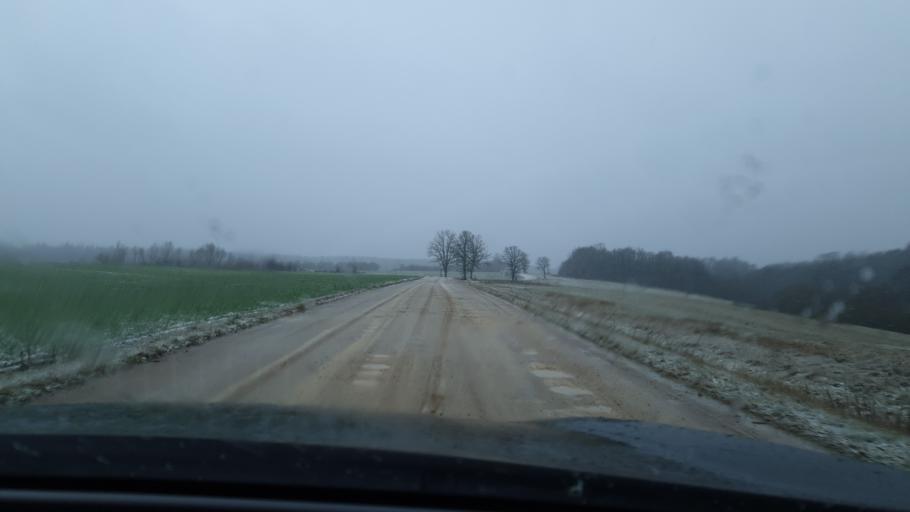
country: LT
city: Jieznas
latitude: 54.5618
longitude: 24.3177
